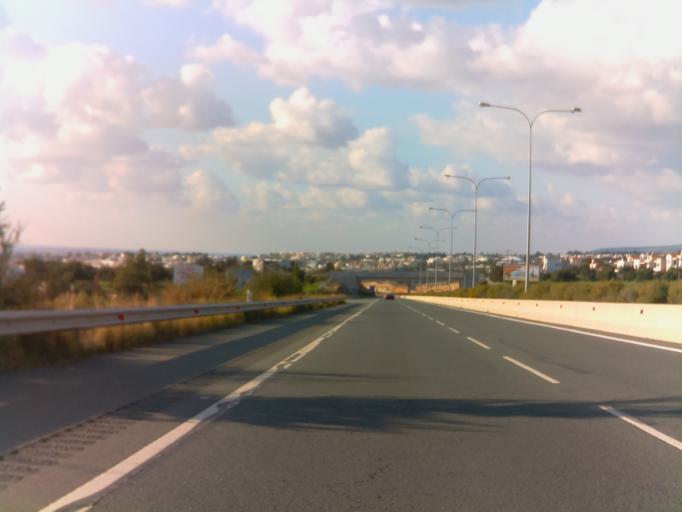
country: CY
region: Pafos
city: Paphos
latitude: 34.7765
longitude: 32.4586
